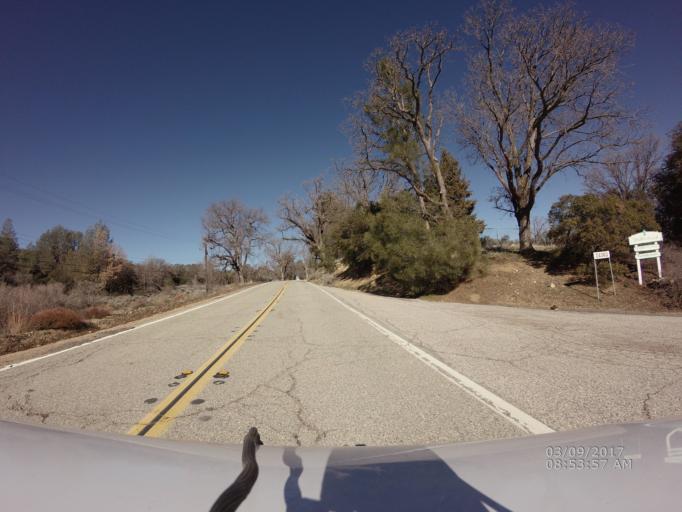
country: US
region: California
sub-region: Los Angeles County
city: Green Valley
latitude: 34.7133
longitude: -118.5617
